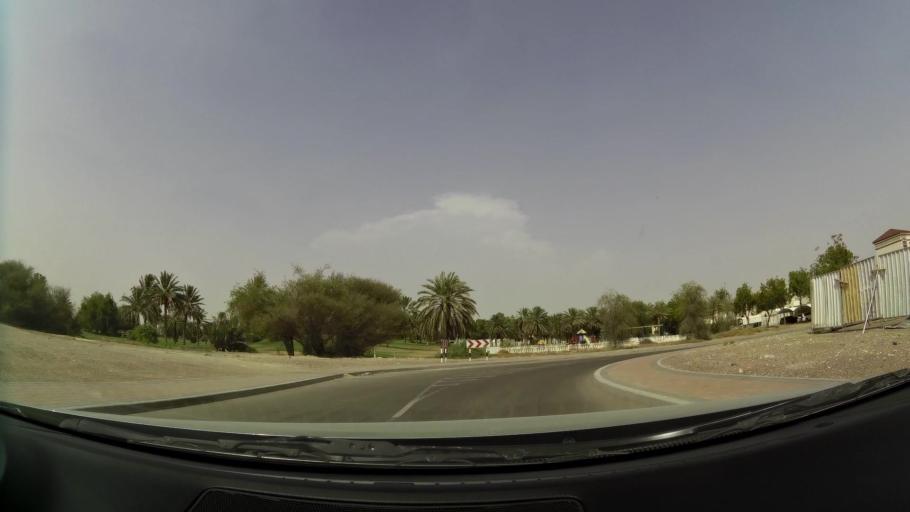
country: AE
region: Abu Dhabi
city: Al Ain
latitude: 24.1947
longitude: 55.6302
